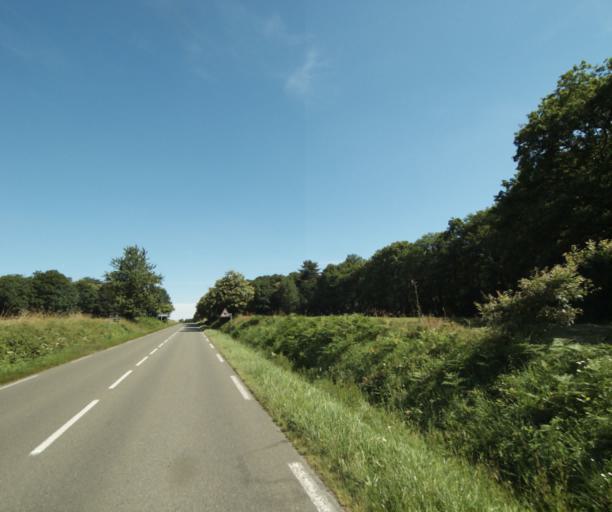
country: FR
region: Pays de la Loire
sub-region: Departement de la Mayenne
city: Laval
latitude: 48.0469
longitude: -0.7842
